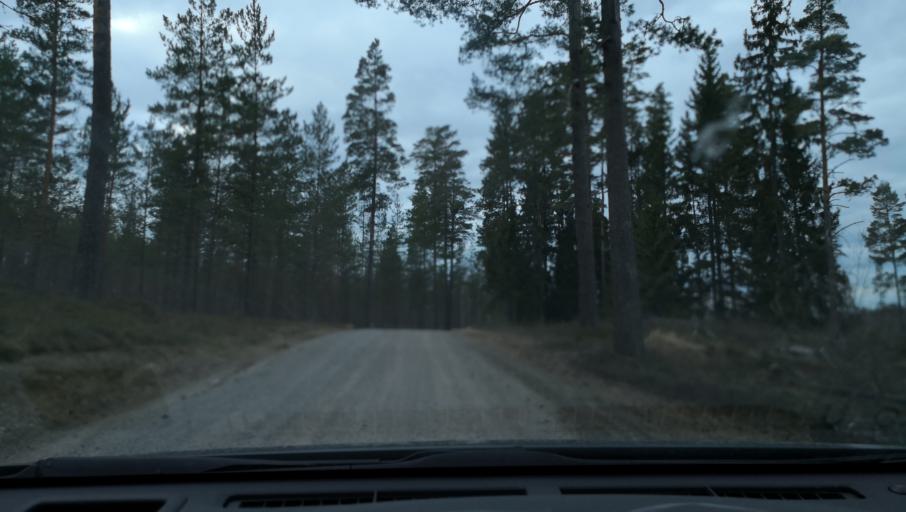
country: SE
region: Soedermanland
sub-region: Katrineholms Kommun
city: Katrineholm
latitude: 59.1326
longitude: 16.1490
